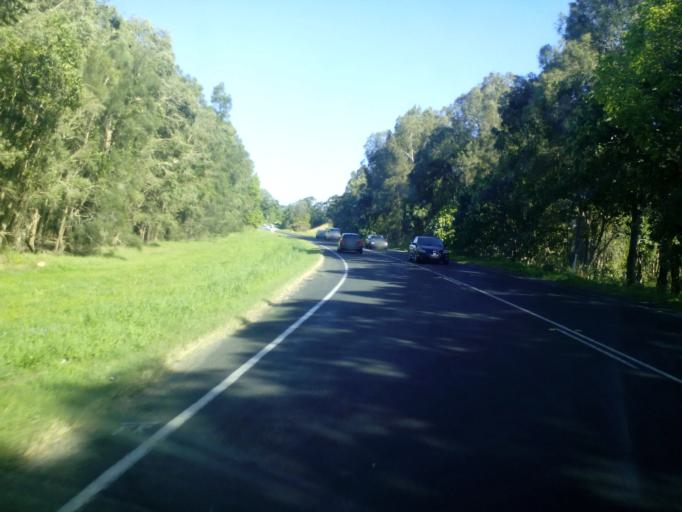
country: AU
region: New South Wales
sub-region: Tweed
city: Kingscliff
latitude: -28.2579
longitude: 153.5599
